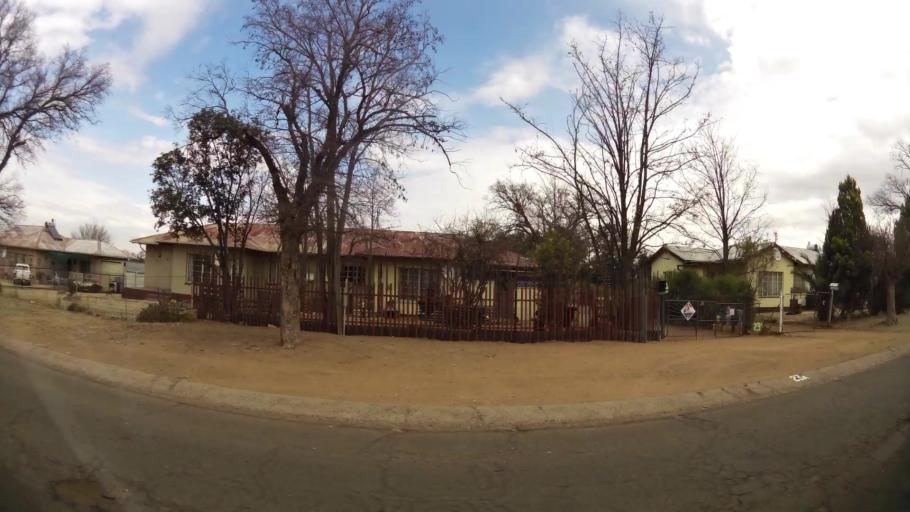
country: ZA
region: Orange Free State
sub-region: Fezile Dabi District Municipality
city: Kroonstad
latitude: -27.6436
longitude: 27.2290
